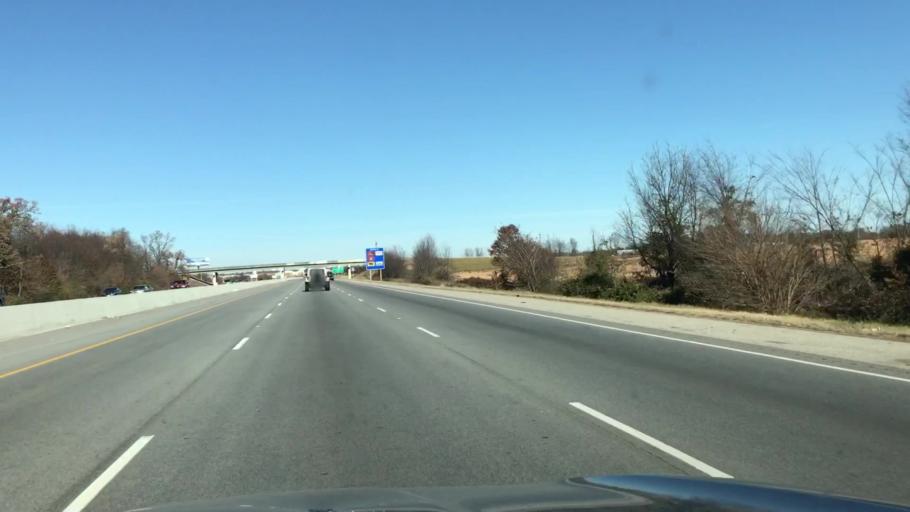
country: US
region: Arkansas
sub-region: Benton County
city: Lowell
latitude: 36.2624
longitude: -94.1502
